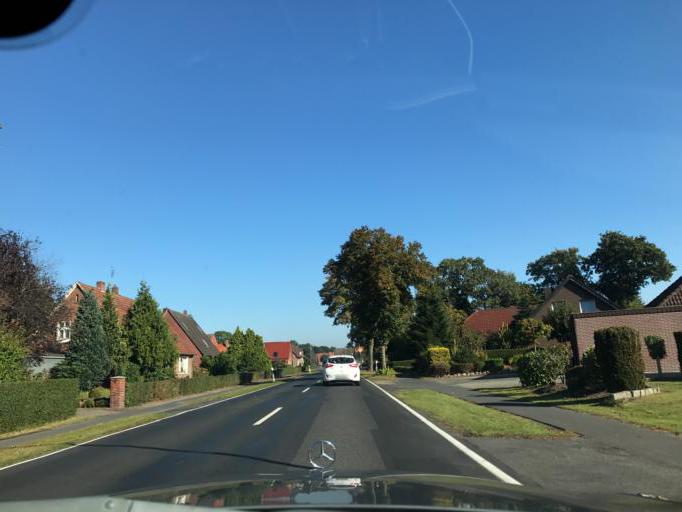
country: DE
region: Lower Saxony
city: Papenburg
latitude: 53.0659
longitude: 7.3418
